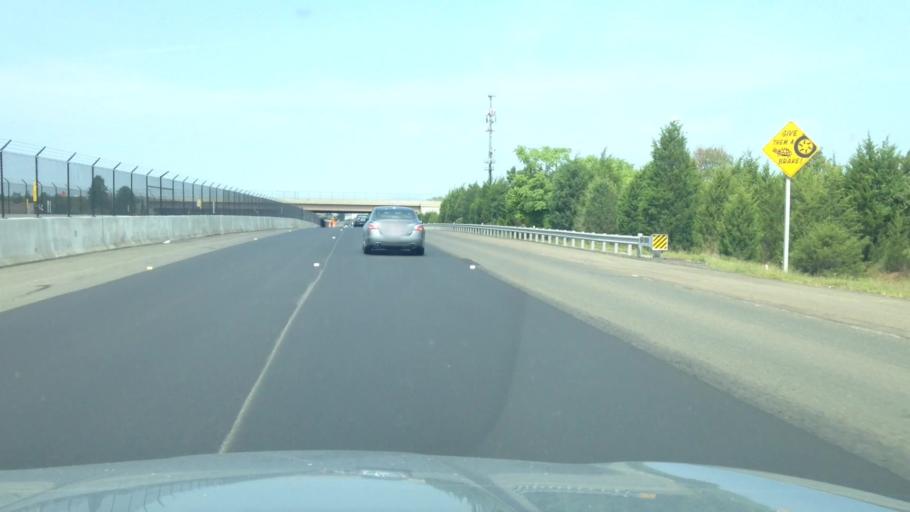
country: US
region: Virginia
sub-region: Loudoun County
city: Sterling
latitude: 38.9962
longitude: -77.4757
